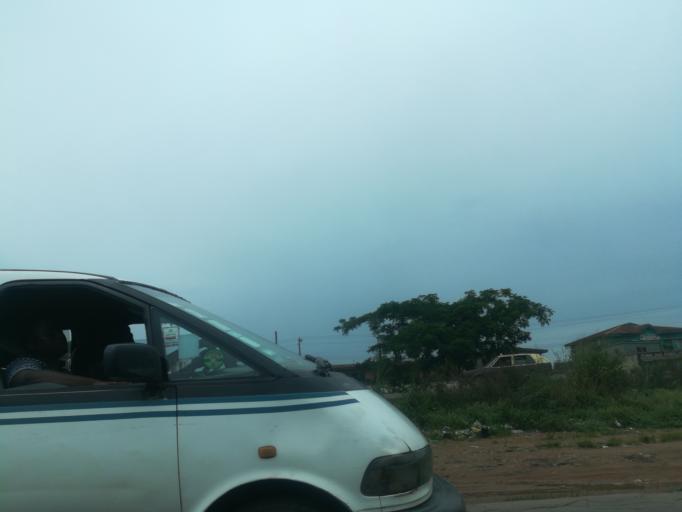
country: NG
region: Oyo
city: Ibadan
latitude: 7.3413
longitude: 3.9085
